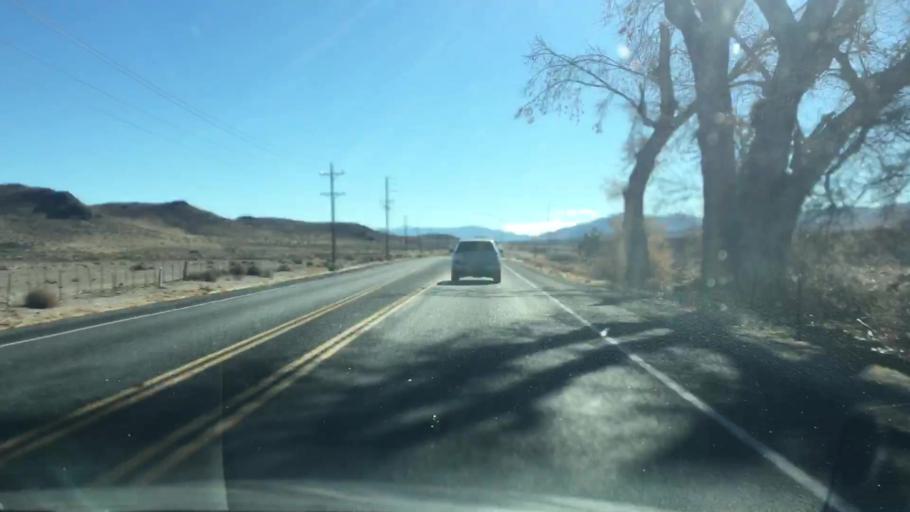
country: US
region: Nevada
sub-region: Lyon County
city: Yerington
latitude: 39.0275
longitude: -119.1816
